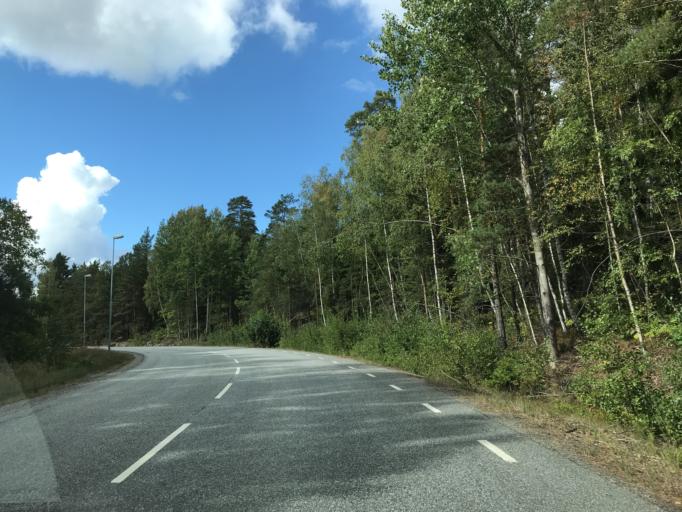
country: SE
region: Stockholm
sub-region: Sollentuna Kommun
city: Sollentuna
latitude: 59.4586
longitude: 17.9623
